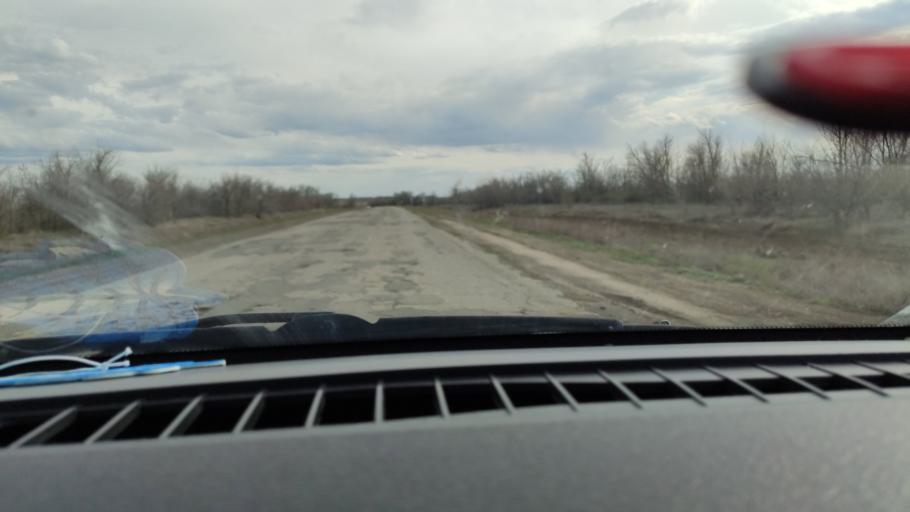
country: RU
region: Saratov
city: Rovnoye
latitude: 50.9627
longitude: 46.1173
